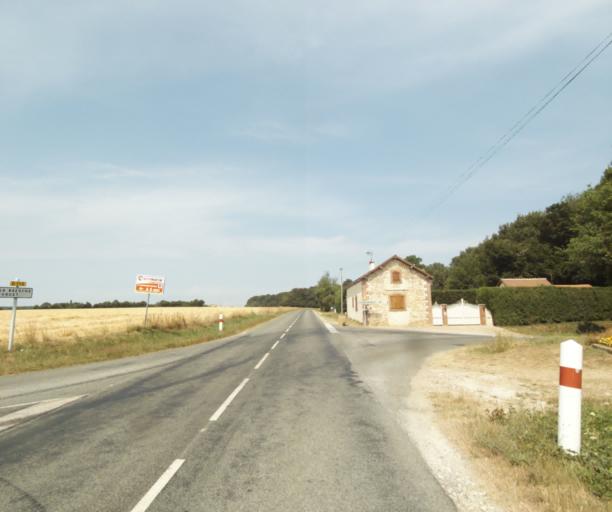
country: FR
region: Centre
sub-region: Departement d'Eure-et-Loir
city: Authon-du-Perche
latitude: 48.1851
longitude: 0.9329
